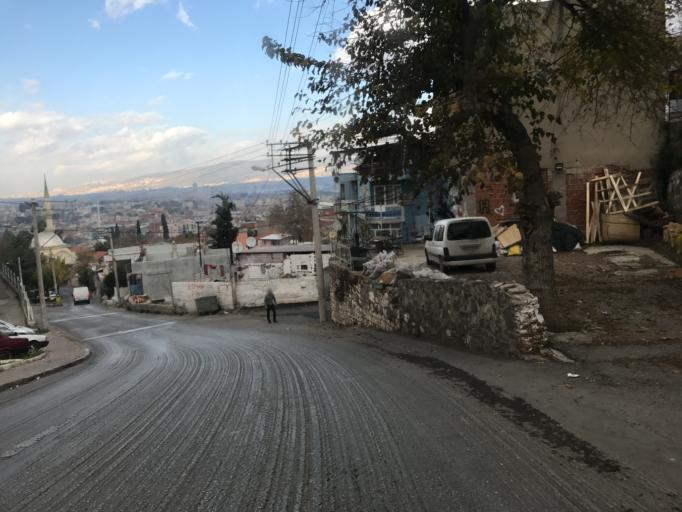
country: TR
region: Izmir
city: Buca
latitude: 38.4117
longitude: 27.1631
